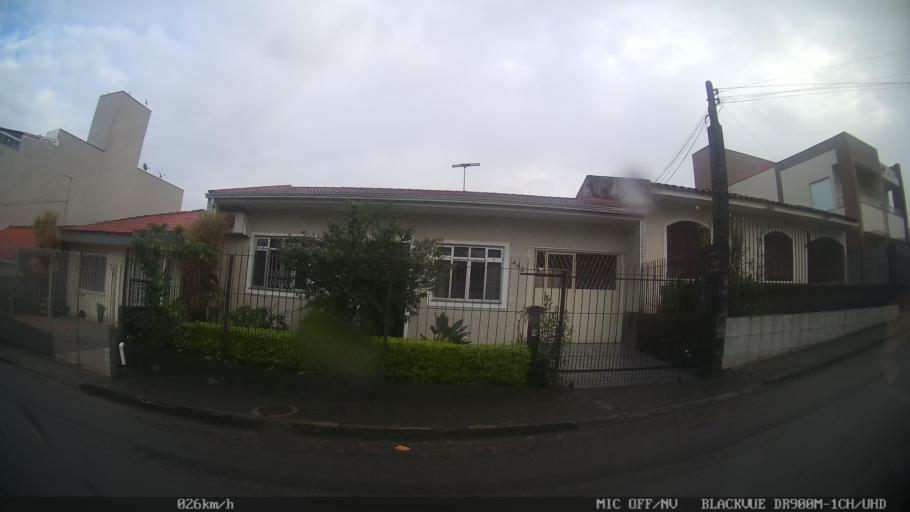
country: BR
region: Santa Catarina
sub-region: Sao Jose
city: Campinas
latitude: -27.5752
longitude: -48.6082
